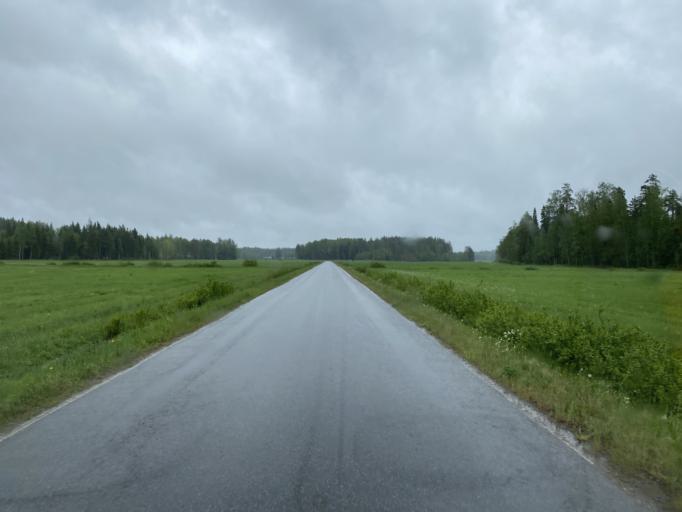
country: FI
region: Haeme
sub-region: Forssa
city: Humppila
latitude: 61.0520
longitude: 23.3442
